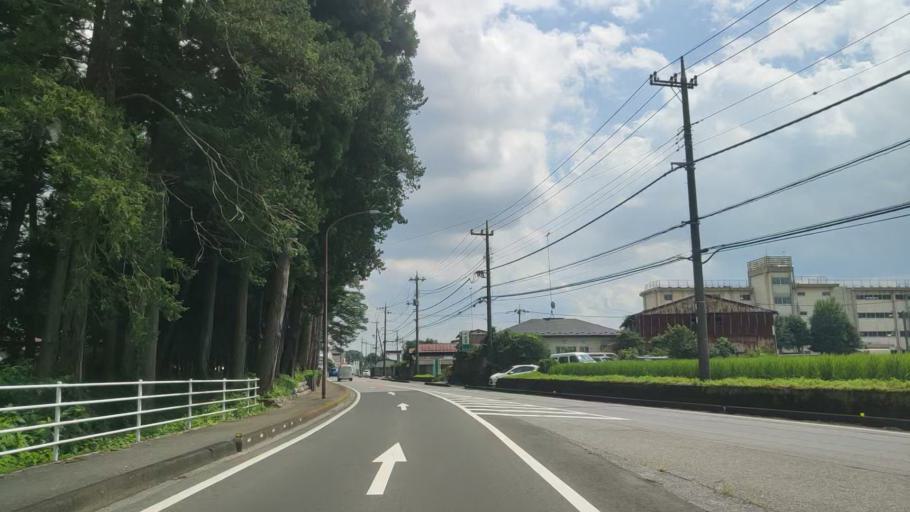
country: JP
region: Tochigi
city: Utsunomiya-shi
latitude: 36.6573
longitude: 139.8403
